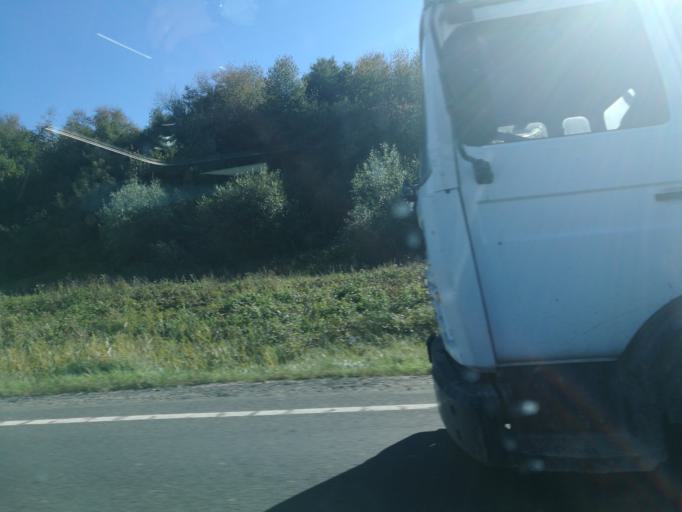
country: RO
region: Brasov
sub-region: Comuna Mandra
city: Mandra
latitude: 45.8226
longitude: 25.0652
